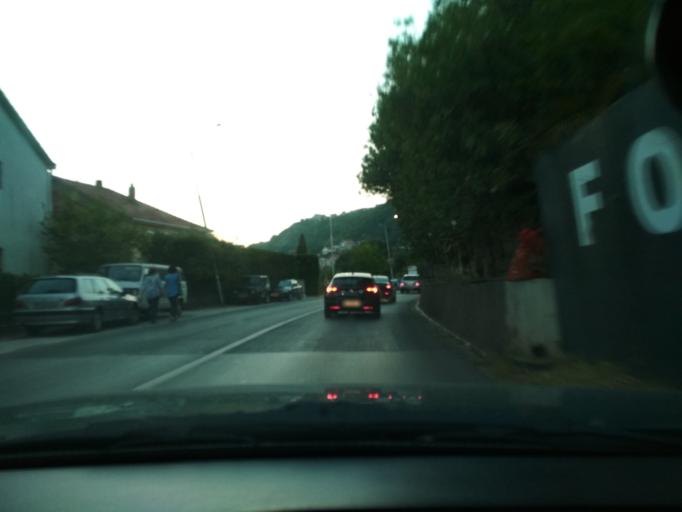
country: ME
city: Igalo
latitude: 42.4587
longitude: 18.5220
